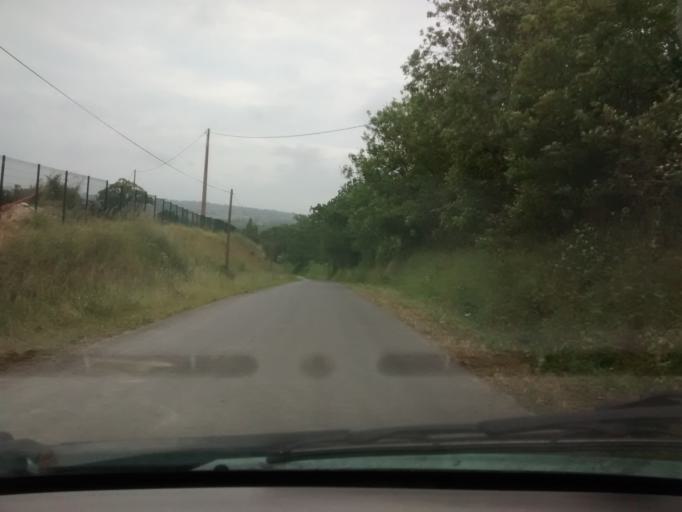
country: FR
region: Lower Normandy
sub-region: Departement de la Manche
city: Saint-Lo
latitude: 49.0985
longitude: -1.0669
